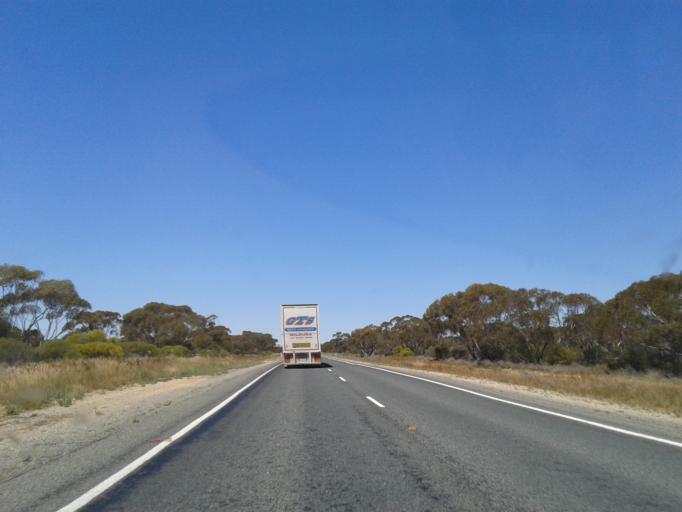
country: AU
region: New South Wales
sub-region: Wentworth
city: Gol Gol
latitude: -34.4982
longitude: 142.5745
